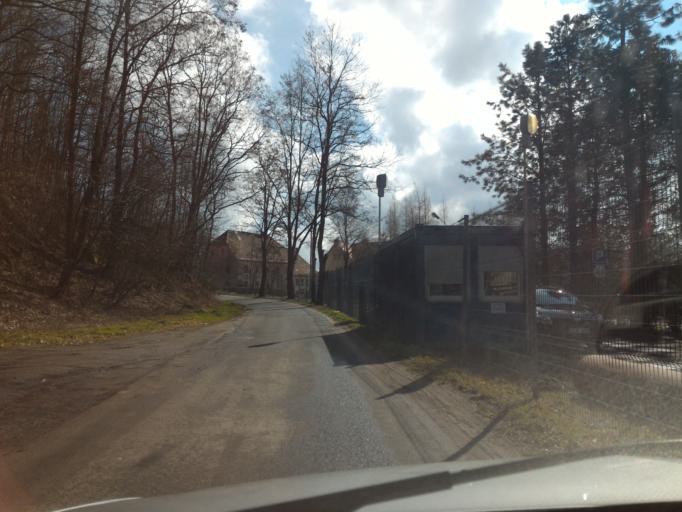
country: DE
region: Saxony
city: Ostritz
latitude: 51.0403
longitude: 14.9854
